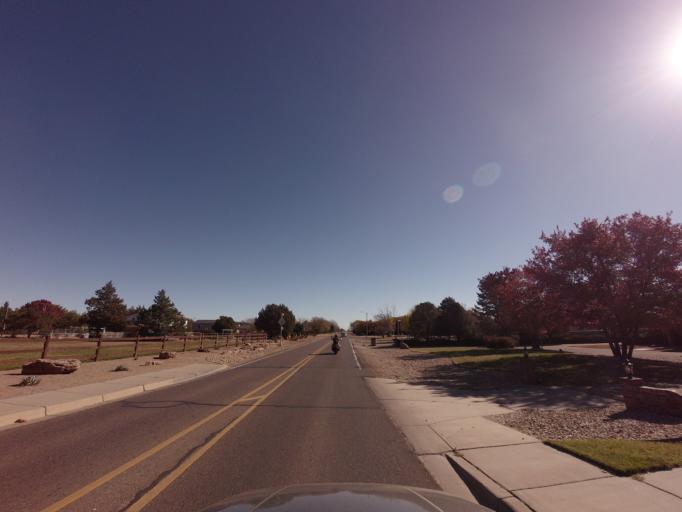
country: US
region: New Mexico
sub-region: Curry County
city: Clovis
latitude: 34.4193
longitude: -103.1775
